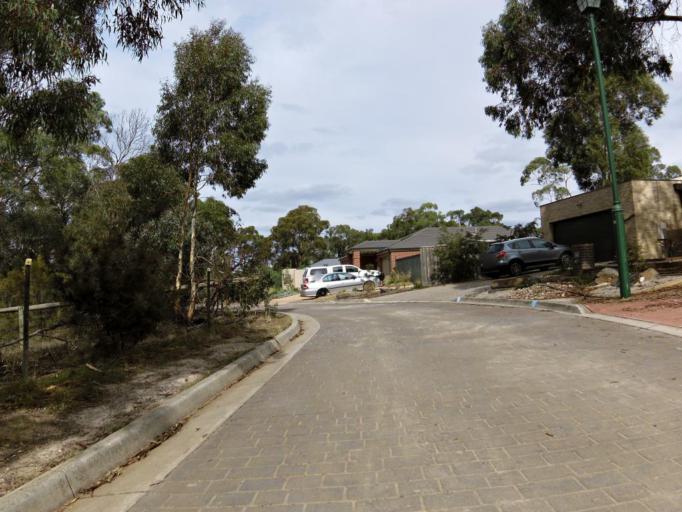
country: AU
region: Victoria
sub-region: Hume
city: Sunbury
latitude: -37.5699
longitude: 144.7126
